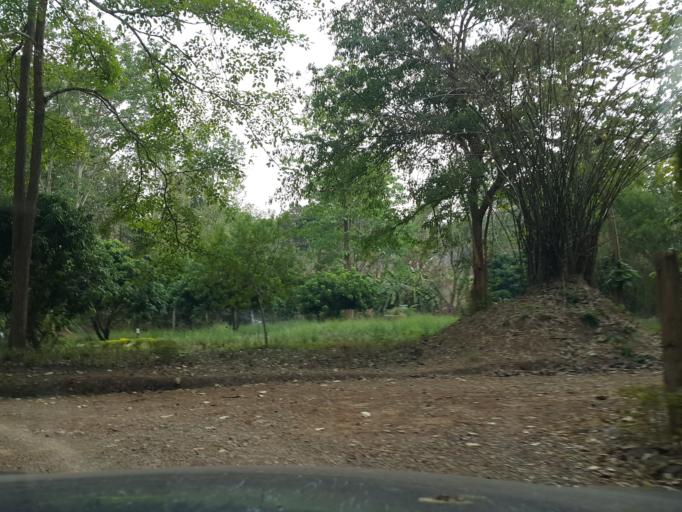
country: TH
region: Lamphun
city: Li
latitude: 17.6133
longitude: 98.9578
